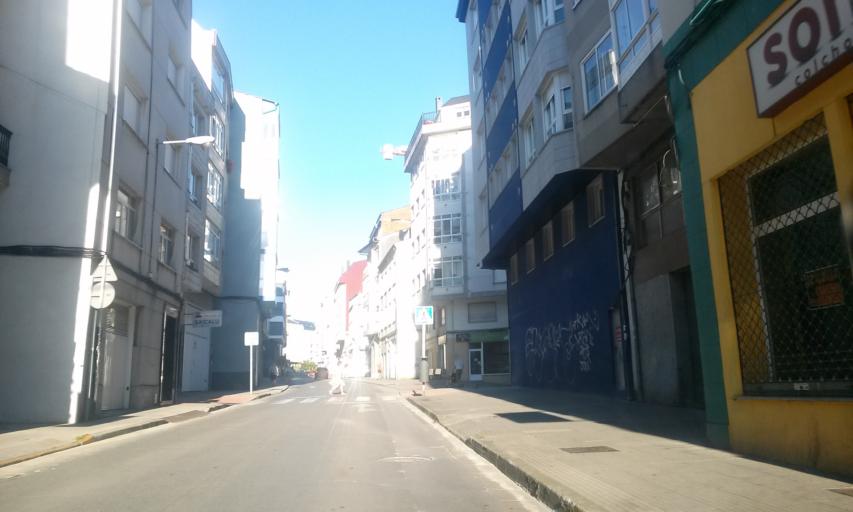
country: ES
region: Galicia
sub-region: Provincia de Lugo
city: Lugo
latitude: 43.0165
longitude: -7.5699
